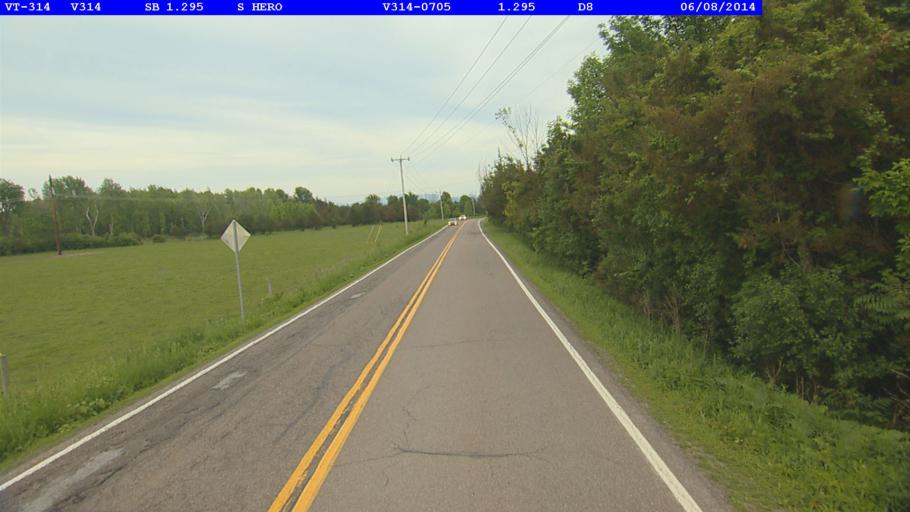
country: US
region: New York
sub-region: Clinton County
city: Cumberland Head
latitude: 44.6751
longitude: -73.3421
